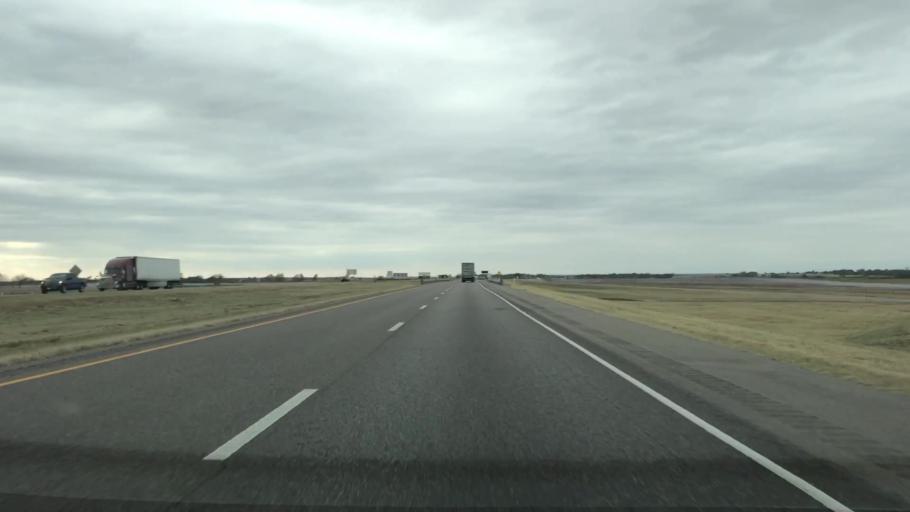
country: US
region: Oklahoma
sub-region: Beckham County
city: Erick
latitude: 35.2283
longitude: -99.9884
